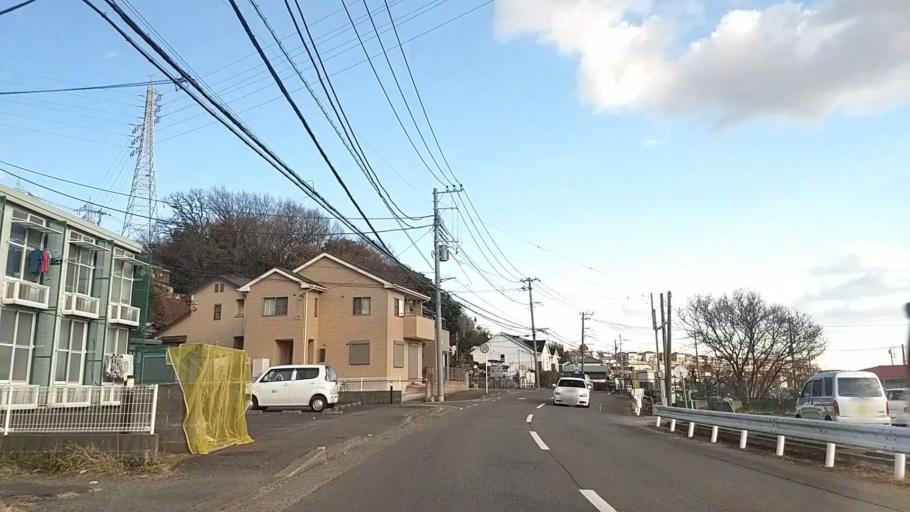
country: JP
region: Kanagawa
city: Atsugi
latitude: 35.4418
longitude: 139.3440
